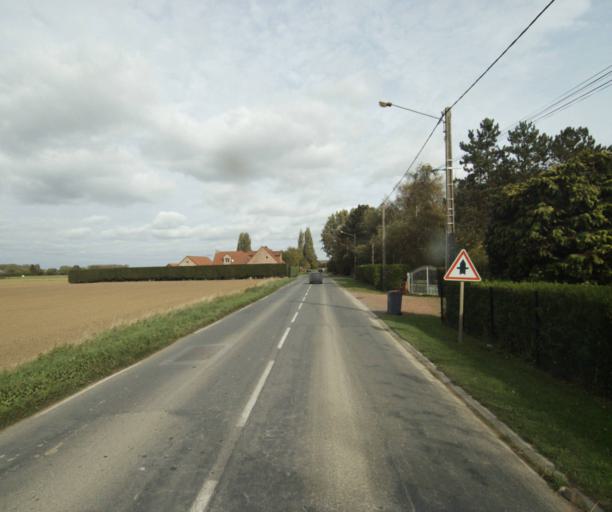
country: FR
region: Nord-Pas-de-Calais
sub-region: Departement du Nord
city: Bois-Grenier
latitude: 50.6548
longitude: 2.8838
